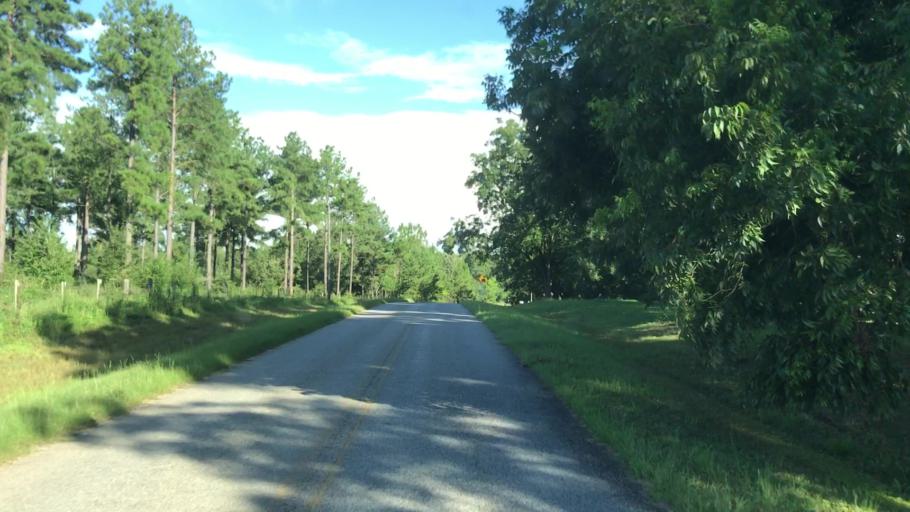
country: US
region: Georgia
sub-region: Jefferson County
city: Wadley
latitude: 32.8013
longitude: -82.3663
